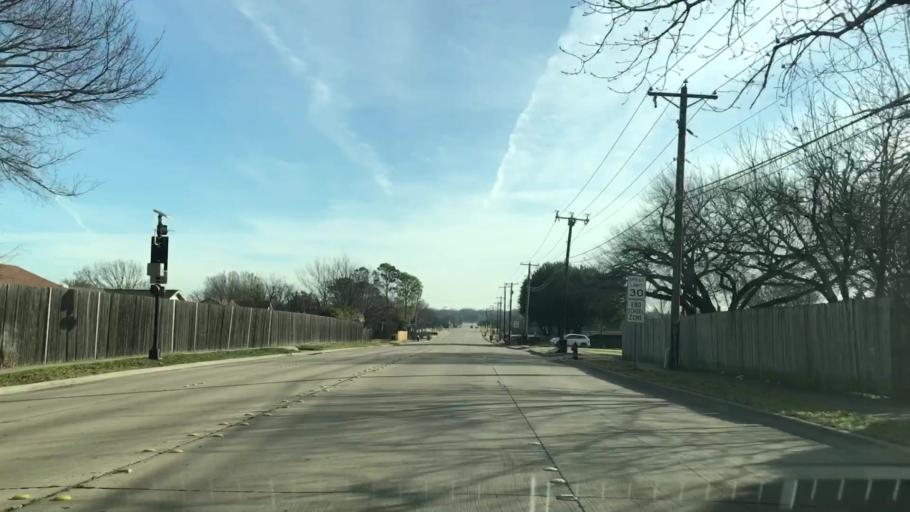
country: US
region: Texas
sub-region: Tarrant County
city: Watauga
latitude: 32.8749
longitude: -97.2297
